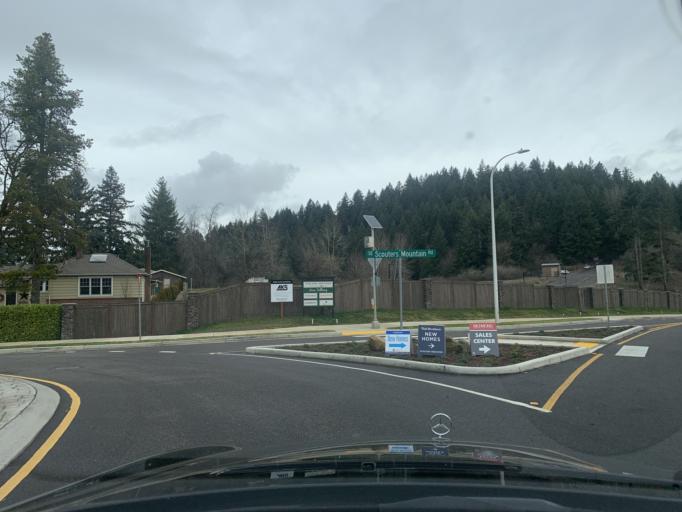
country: US
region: Oregon
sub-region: Clackamas County
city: Happy Valley
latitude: 45.4410
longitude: -122.5120
